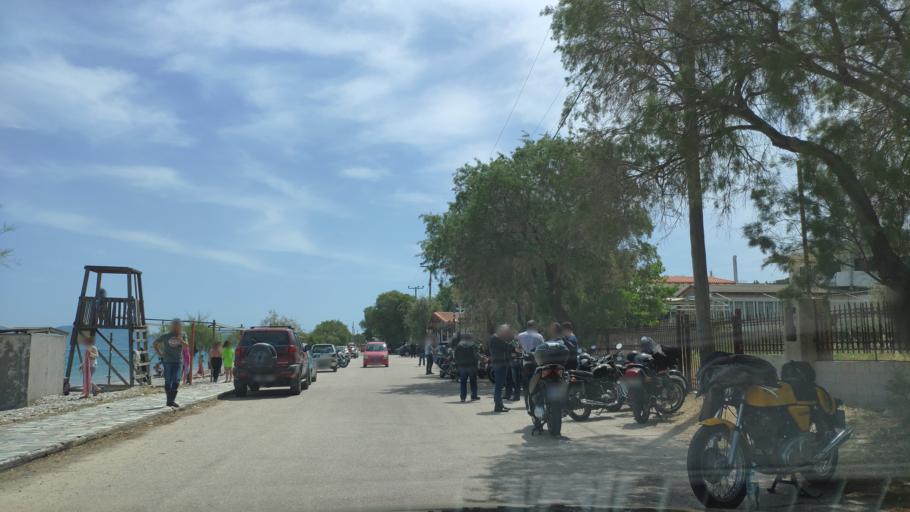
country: GR
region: Attica
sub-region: Nomarchia Anatolikis Attikis
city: Grammatiko
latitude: 38.2629
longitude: 23.9774
